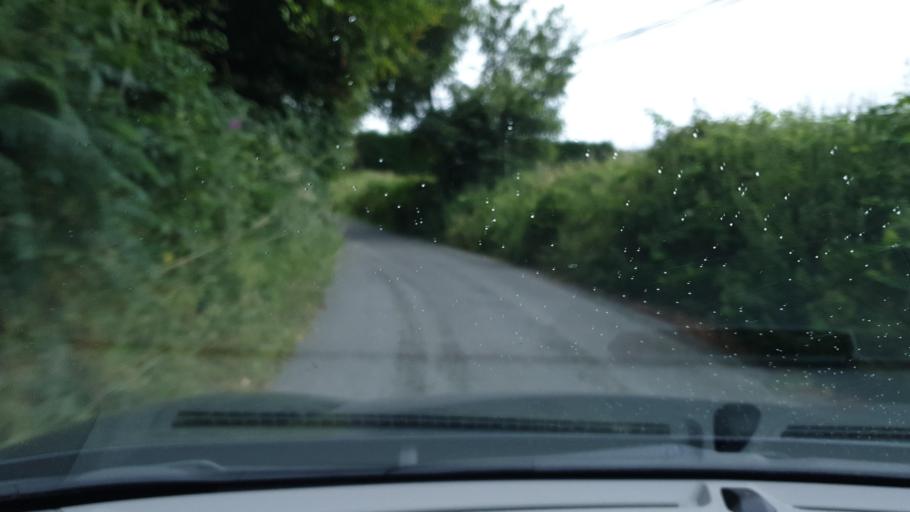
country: IE
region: Leinster
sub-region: South Dublin
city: Rathcoole
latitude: 53.2204
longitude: -6.4873
